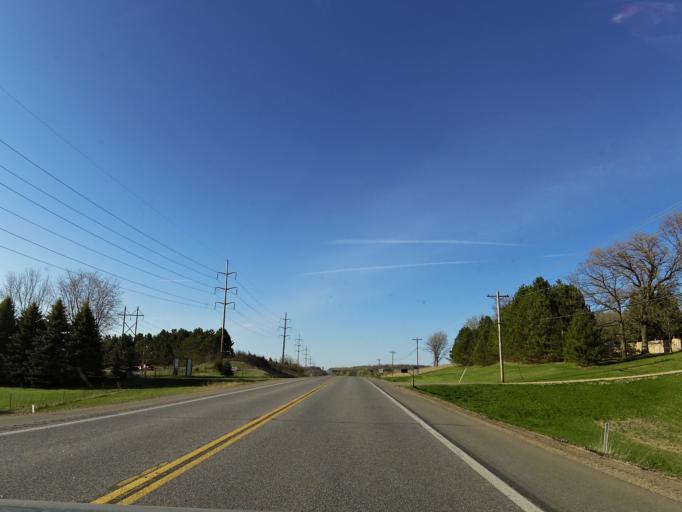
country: US
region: Minnesota
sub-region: Scott County
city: Elko New Market
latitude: 44.6002
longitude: -93.2933
